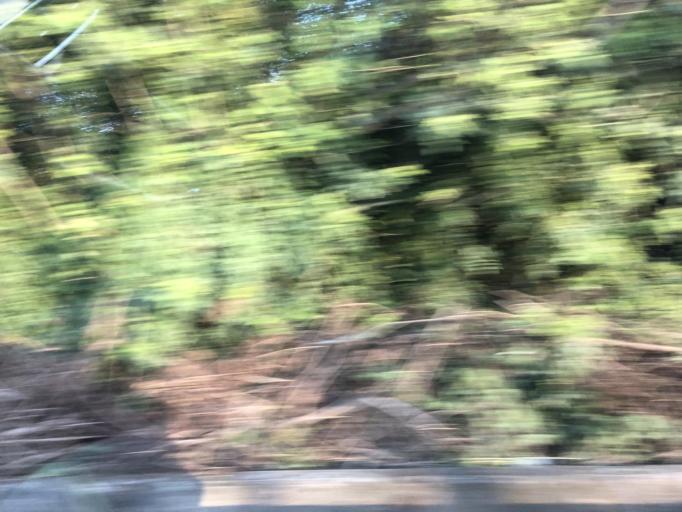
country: TW
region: Taiwan
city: Xinying
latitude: 23.1510
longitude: 120.2744
